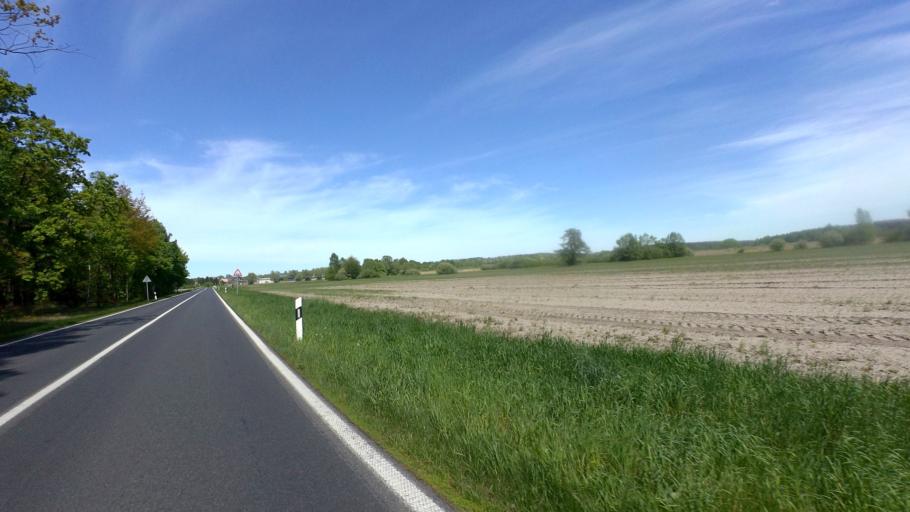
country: DE
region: Brandenburg
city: Sperenberg
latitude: 52.1268
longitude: 13.3670
